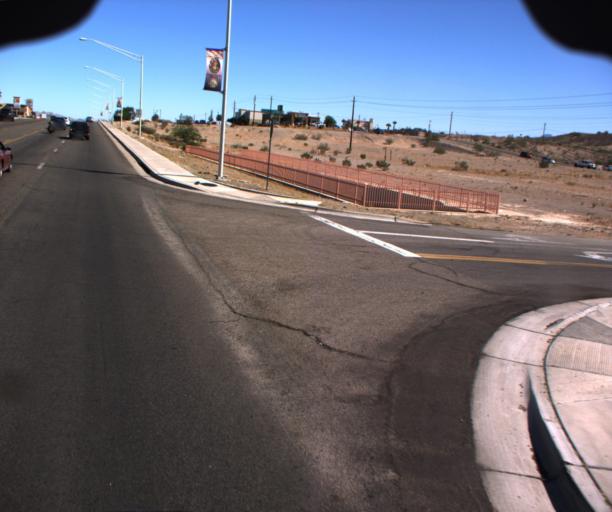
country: US
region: Arizona
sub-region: Mohave County
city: Bullhead City
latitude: 35.0859
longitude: -114.5978
